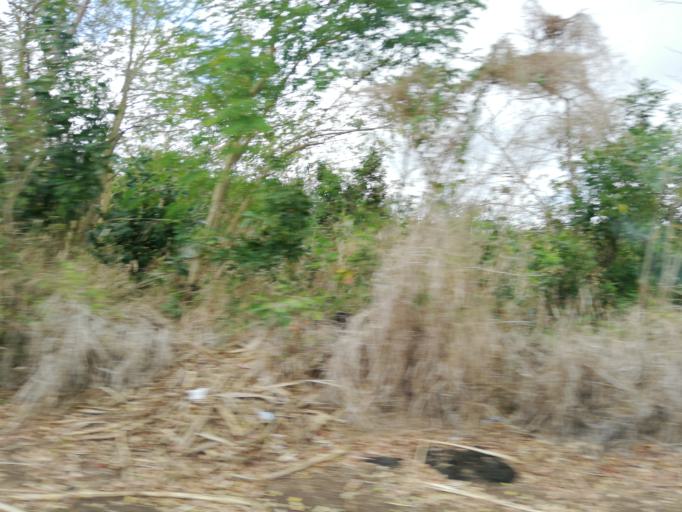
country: MU
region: Pamplemousses
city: Arsenal
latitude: -20.0902
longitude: 57.5440
